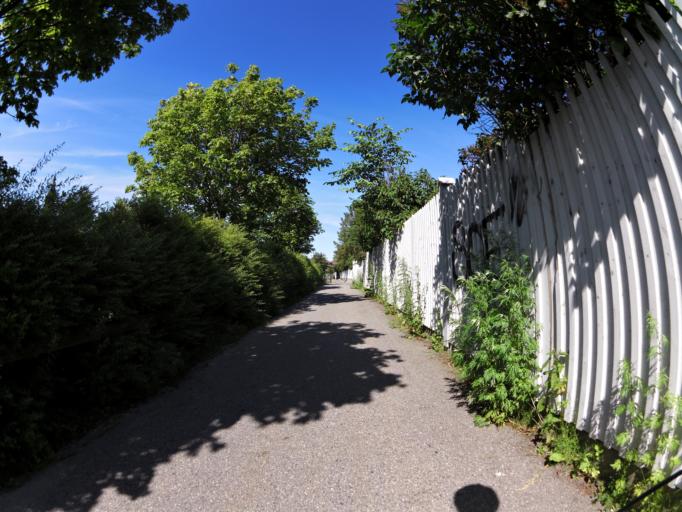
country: NO
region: Ostfold
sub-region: Fredrikstad
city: Fredrikstad
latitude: 59.2205
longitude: 10.9493
